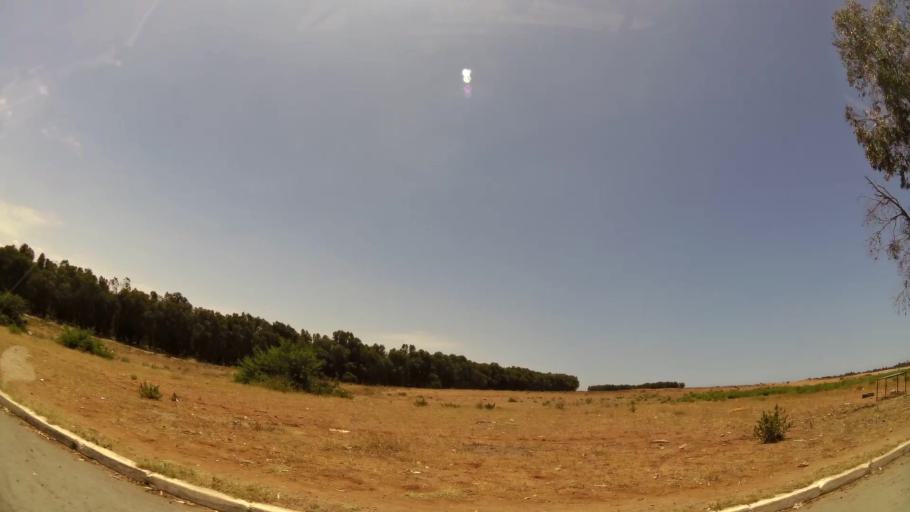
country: MA
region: Gharb-Chrarda-Beni Hssen
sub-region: Kenitra Province
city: Kenitra
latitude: 34.2485
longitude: -6.6233
